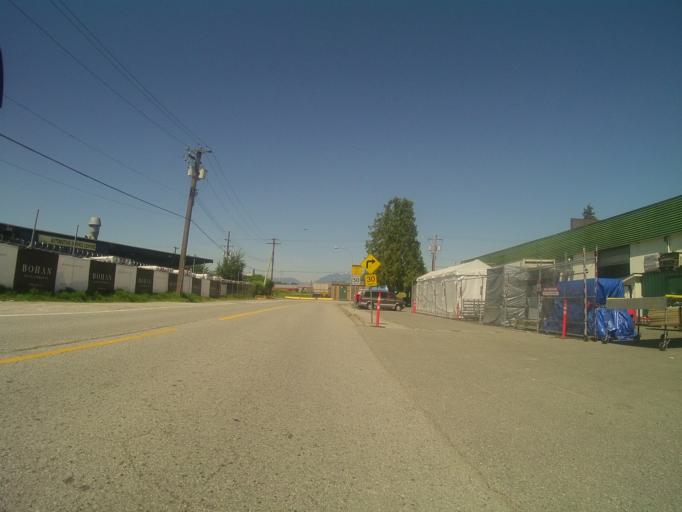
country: CA
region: British Columbia
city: Richmond
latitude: 49.1971
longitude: -123.1027
